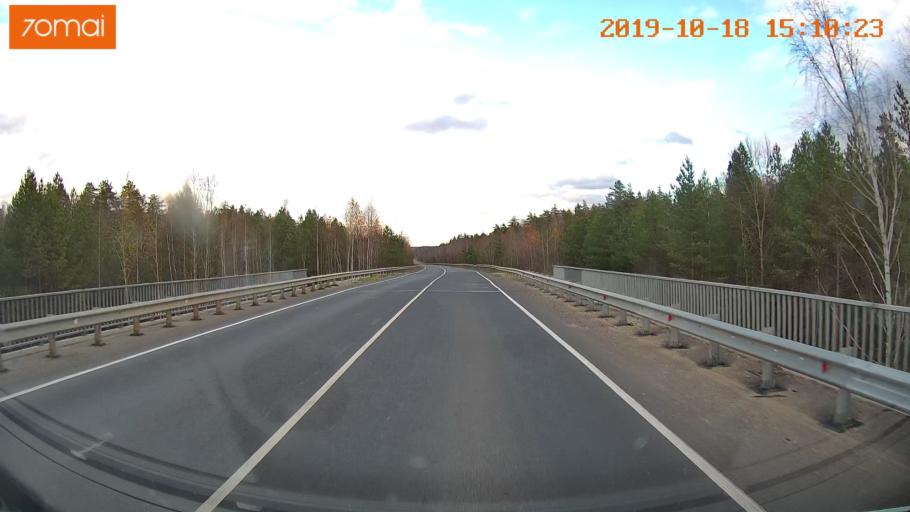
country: RU
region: Vladimir
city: Gus'-Khrustal'nyy
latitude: 55.5677
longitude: 40.6434
